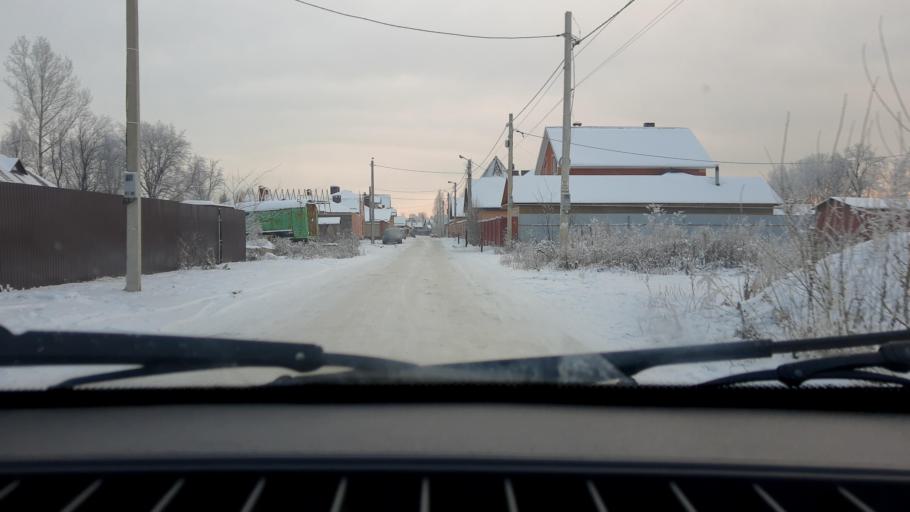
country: RU
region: Bashkortostan
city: Ufa
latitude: 54.6619
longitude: 55.9248
